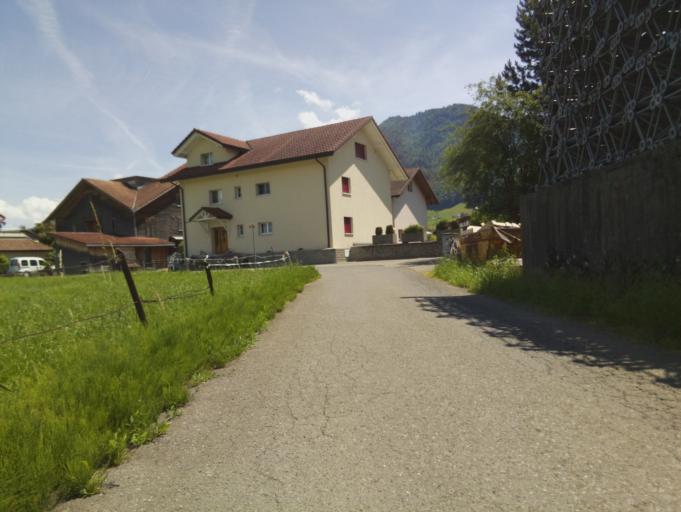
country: CH
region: Schwyz
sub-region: Bezirk March
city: Schubelbach
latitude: 47.1789
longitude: 8.8935
